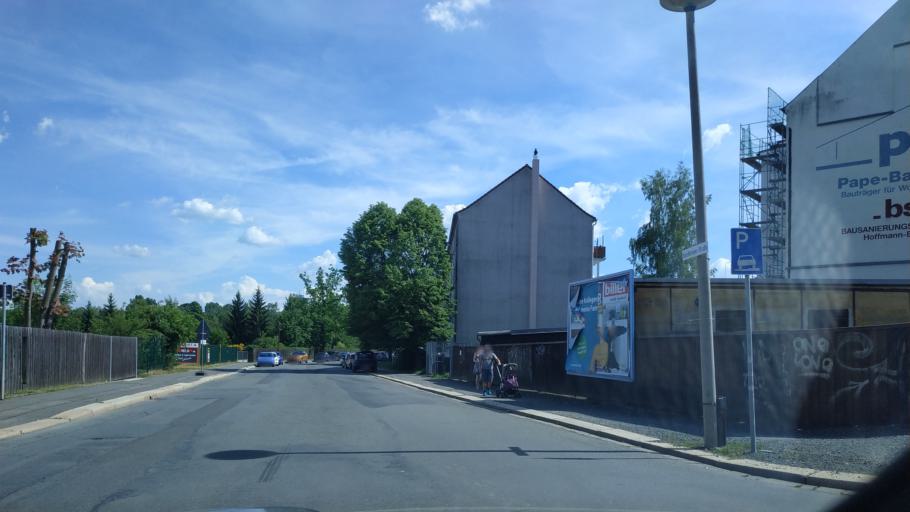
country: DE
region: Saxony
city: Plauen
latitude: 50.5154
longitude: 12.1319
